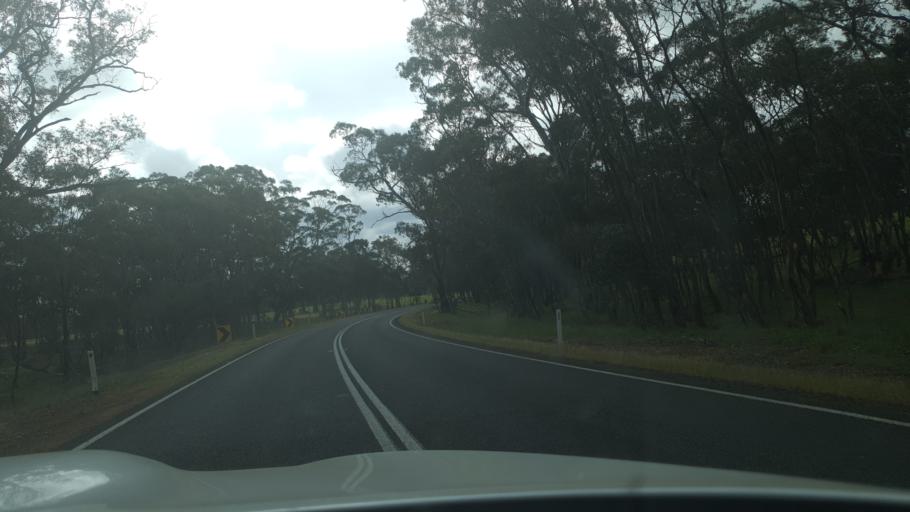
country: AU
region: Victoria
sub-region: Central Goldfields
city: Maryborough
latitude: -37.2034
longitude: 143.7086
